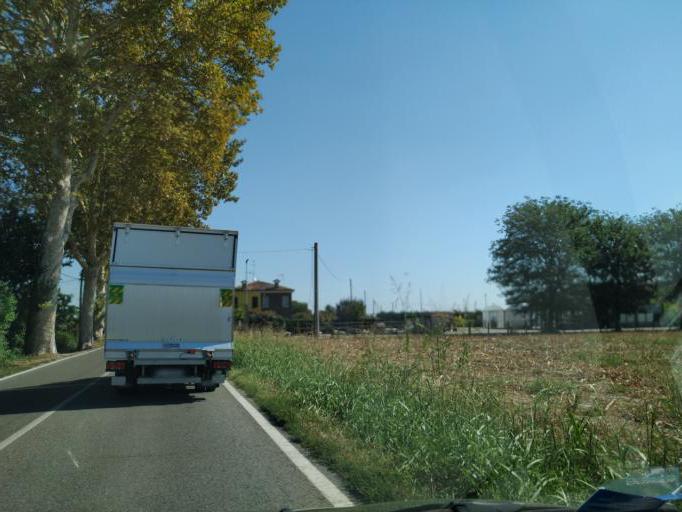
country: IT
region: Emilia-Romagna
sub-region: Provincia di Ferrara
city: La Saletta-Tamara
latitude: 44.8844
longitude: 11.7861
